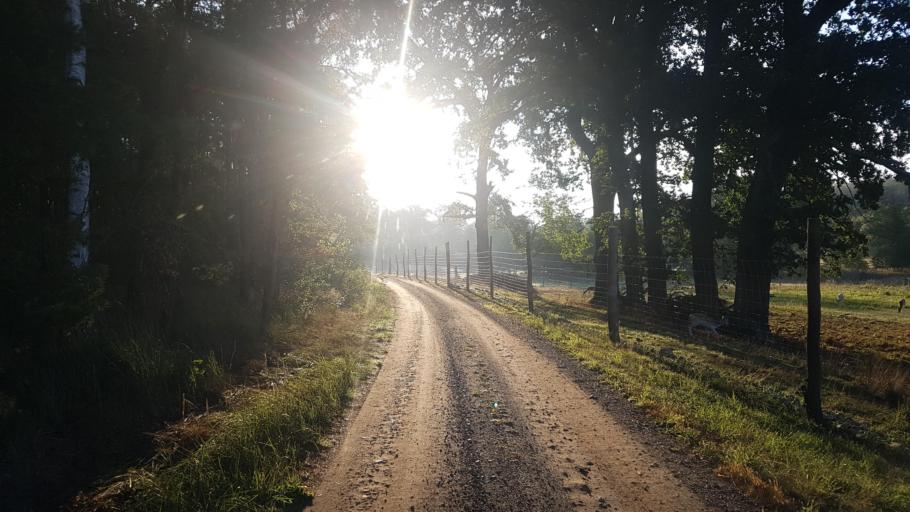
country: DE
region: Brandenburg
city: Hohenbucko
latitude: 51.7921
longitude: 13.4598
